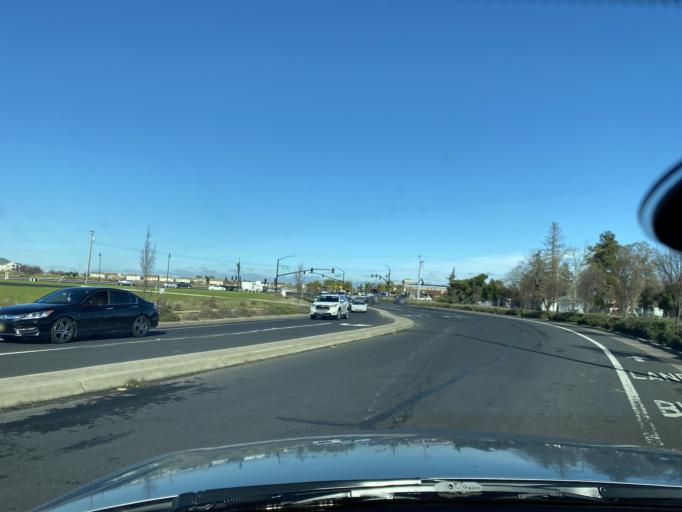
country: US
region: California
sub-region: Sacramento County
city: Laguna
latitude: 38.4365
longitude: -121.3976
